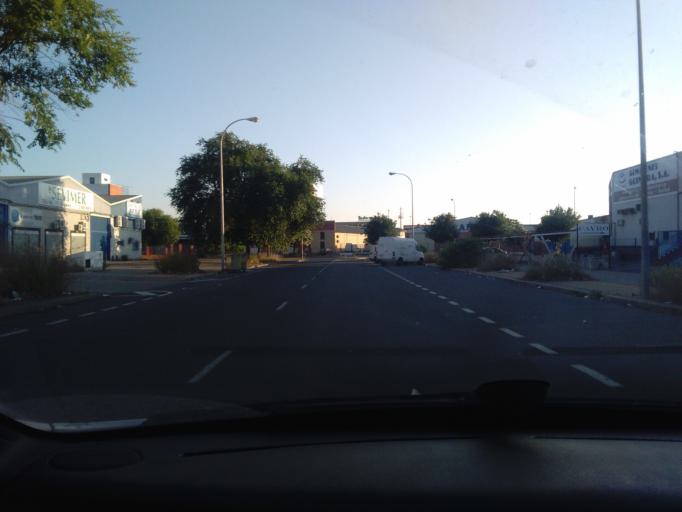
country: ES
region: Andalusia
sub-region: Provincia de Sevilla
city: Sevilla
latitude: 37.3929
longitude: -5.9403
